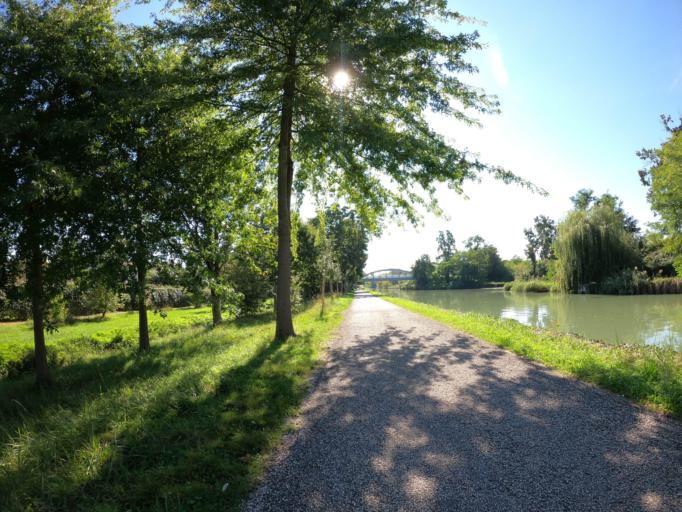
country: FR
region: Aquitaine
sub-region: Departement du Lot-et-Garonne
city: Bon-Encontre
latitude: 44.1797
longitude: 0.6617
